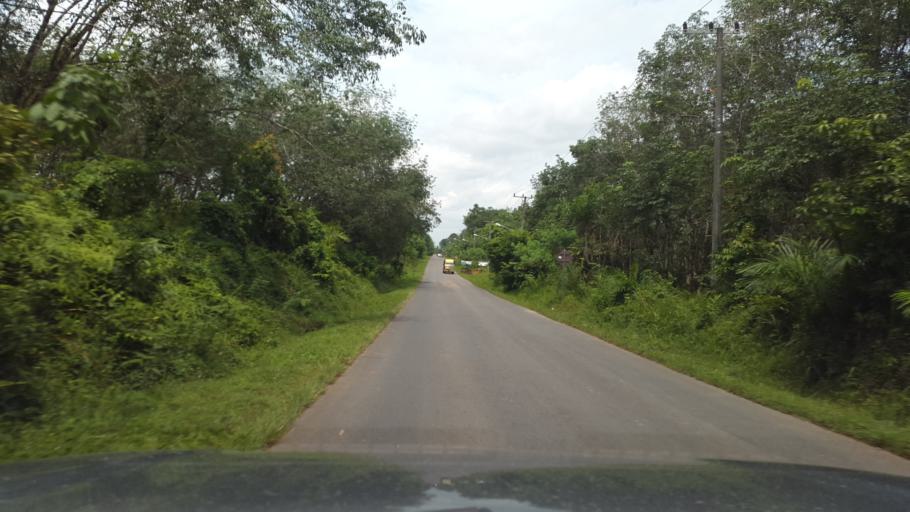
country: ID
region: South Sumatra
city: Gunungmegang Dalam
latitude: -3.3665
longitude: 103.9403
